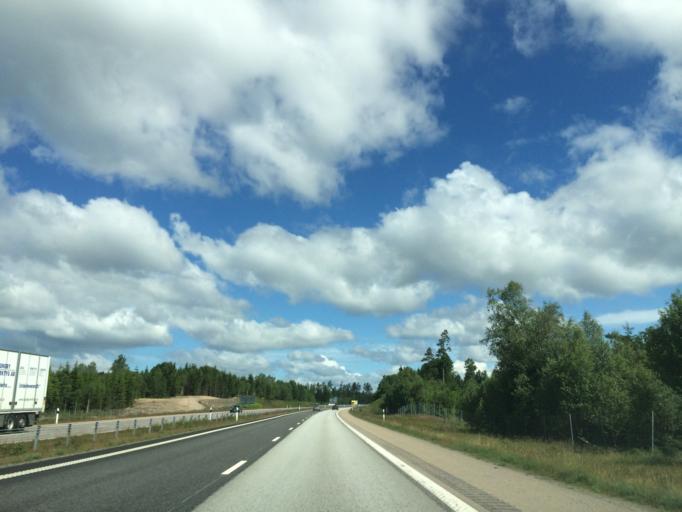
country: SE
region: Kronoberg
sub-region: Markaryds Kommun
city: Stromsnasbruk
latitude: 56.5721
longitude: 13.7209
